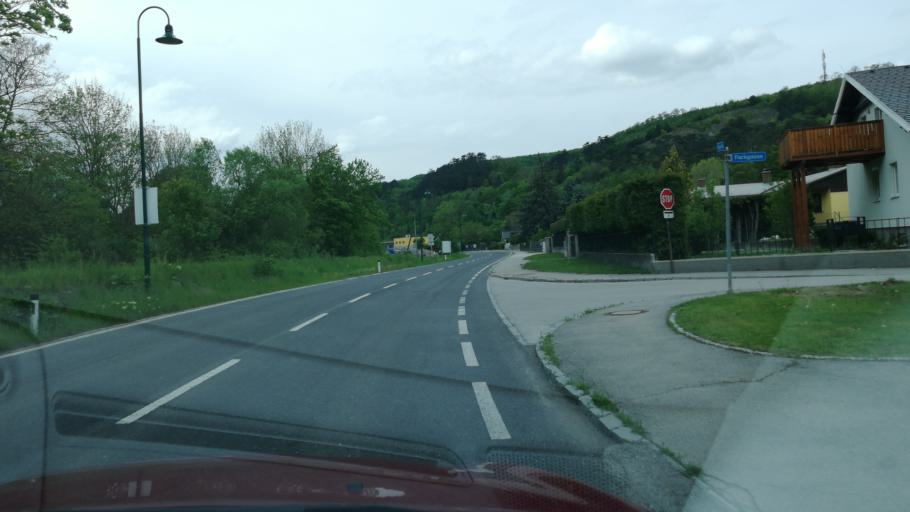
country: AT
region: Lower Austria
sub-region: Politischer Bezirk Baden
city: Alland
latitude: 48.0585
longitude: 16.0746
